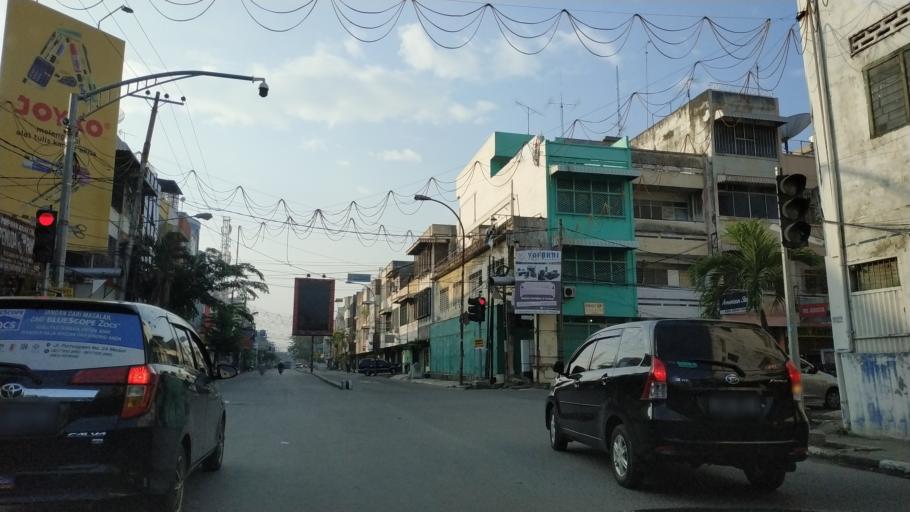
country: ID
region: North Sumatra
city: Medan
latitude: 3.5851
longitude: 98.6919
